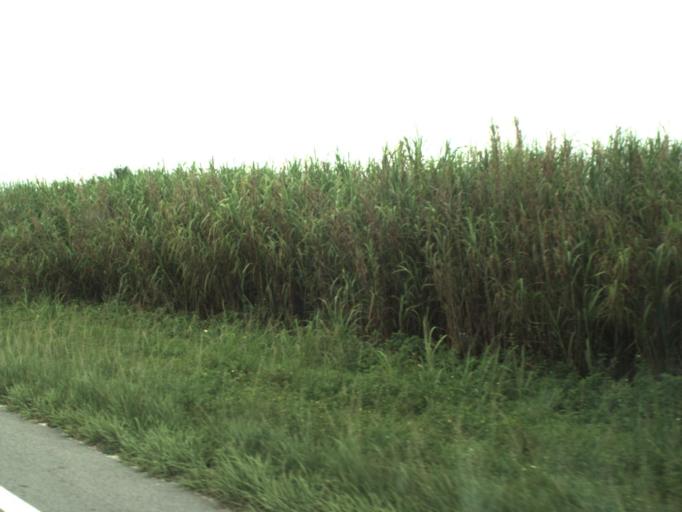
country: US
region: Florida
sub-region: Miami-Dade County
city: The Hammocks
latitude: 25.6746
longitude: -80.4813
